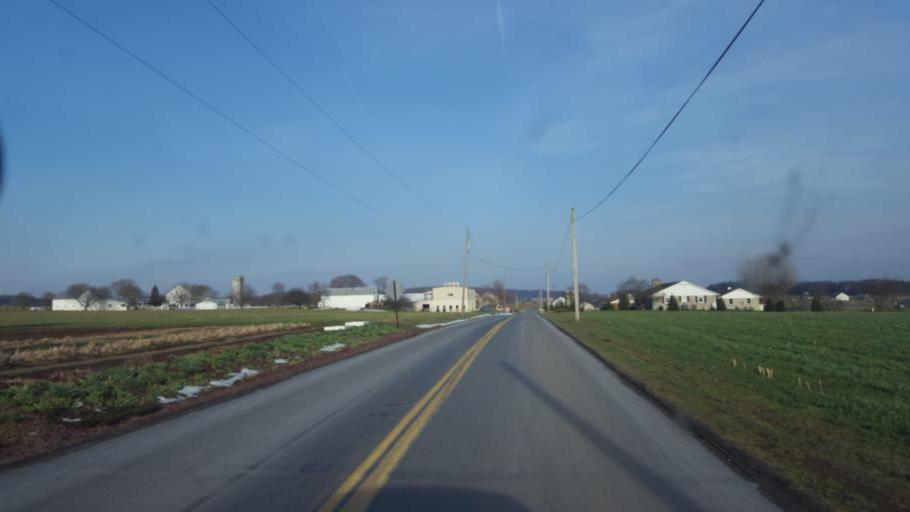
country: US
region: Pennsylvania
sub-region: Lancaster County
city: Intercourse
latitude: 40.0584
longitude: -76.1132
